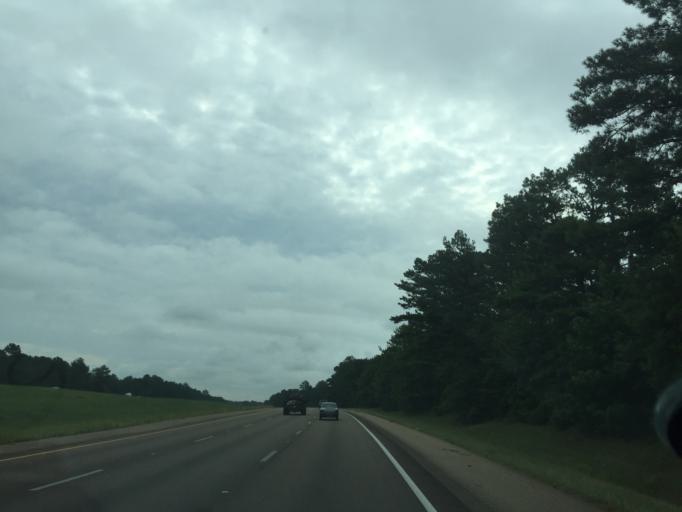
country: US
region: Mississippi
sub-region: Rankin County
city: Pearl
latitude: 32.2655
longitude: -90.1050
